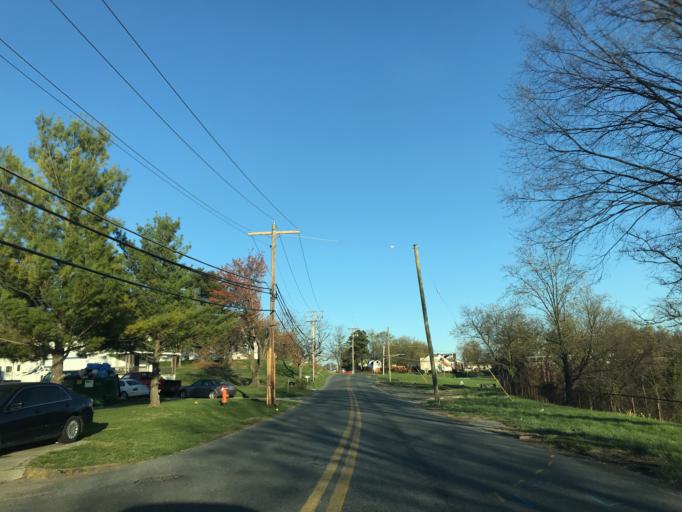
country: US
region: Maryland
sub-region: Baltimore County
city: Rosedale
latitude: 39.3327
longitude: -76.5280
